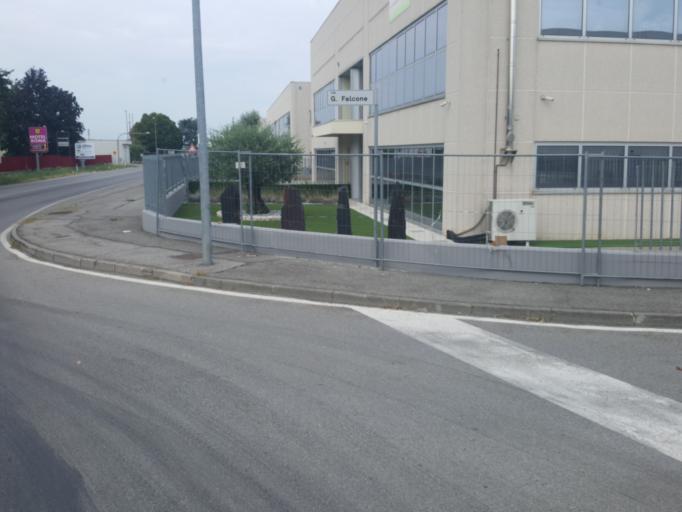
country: IT
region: Lombardy
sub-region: Provincia di Monza e Brianza
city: Cavenago di Brianza
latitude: 45.5805
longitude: 9.4016
